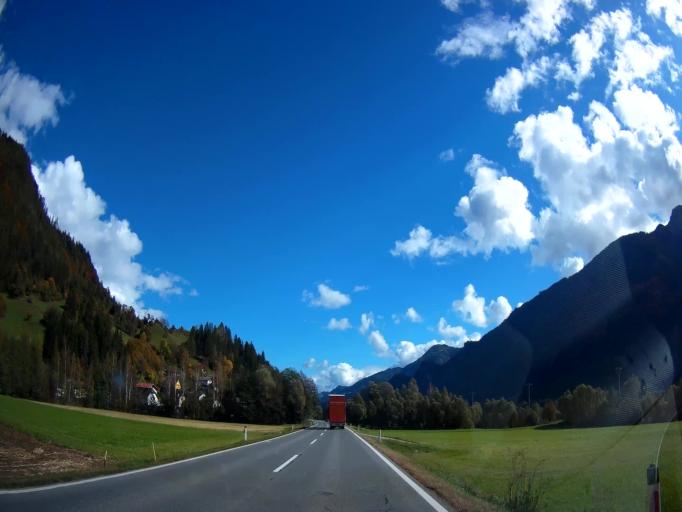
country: AT
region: Carinthia
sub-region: Politischer Bezirk Spittal an der Drau
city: Dellach im Drautal
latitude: 46.7396
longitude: 13.0565
